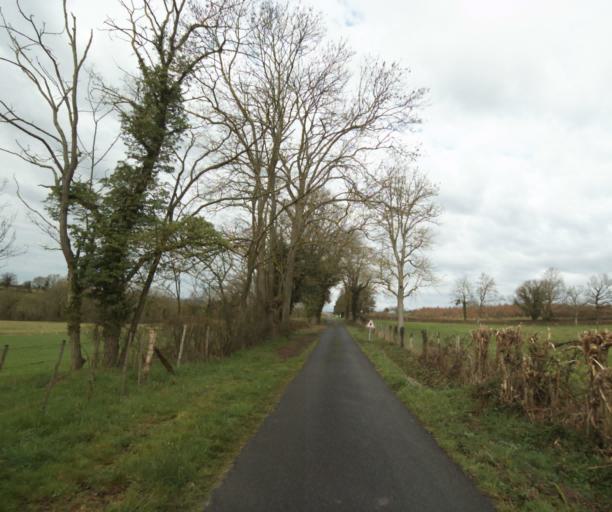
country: FR
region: Auvergne
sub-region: Departement de l'Allier
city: Toulon-sur-Allier
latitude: 46.5140
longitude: 3.3733
